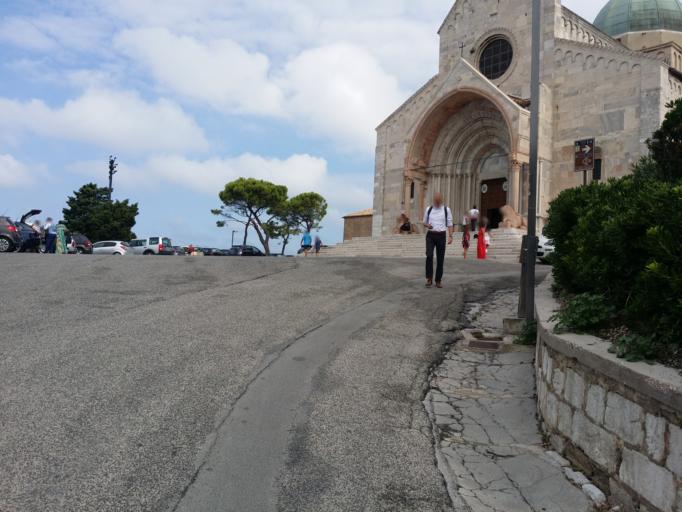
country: IT
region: The Marches
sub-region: Provincia di Ancona
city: Le Grazie di Ancona
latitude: 43.6249
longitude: 13.5103
